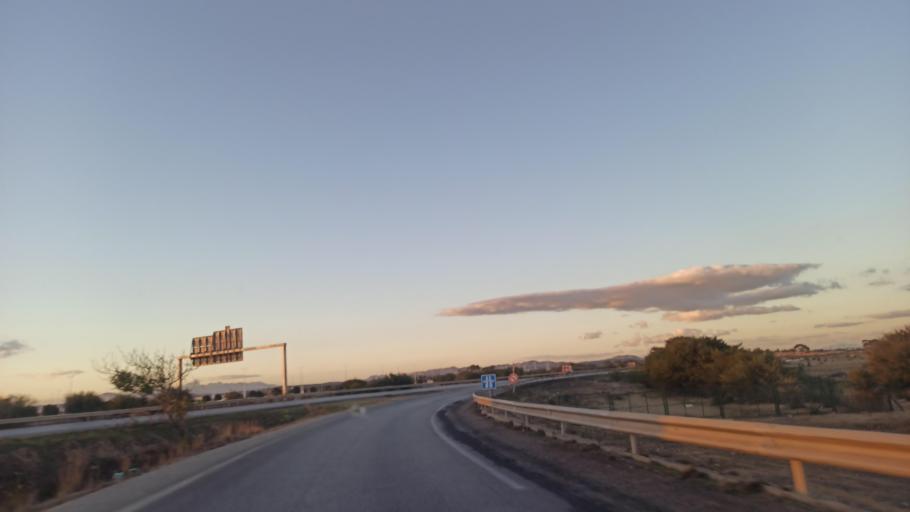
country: TN
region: Susah
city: Harqalah
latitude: 36.1092
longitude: 10.4055
